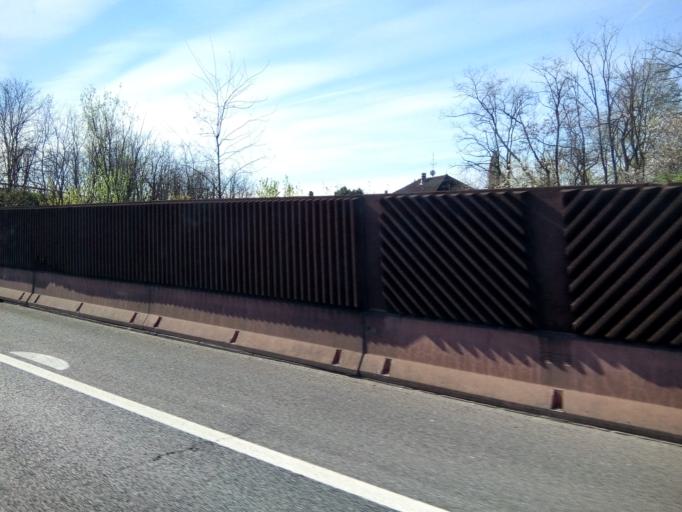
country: IT
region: Lombardy
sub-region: Citta metropolitana di Milano
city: Arese
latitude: 45.5439
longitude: 9.0680
